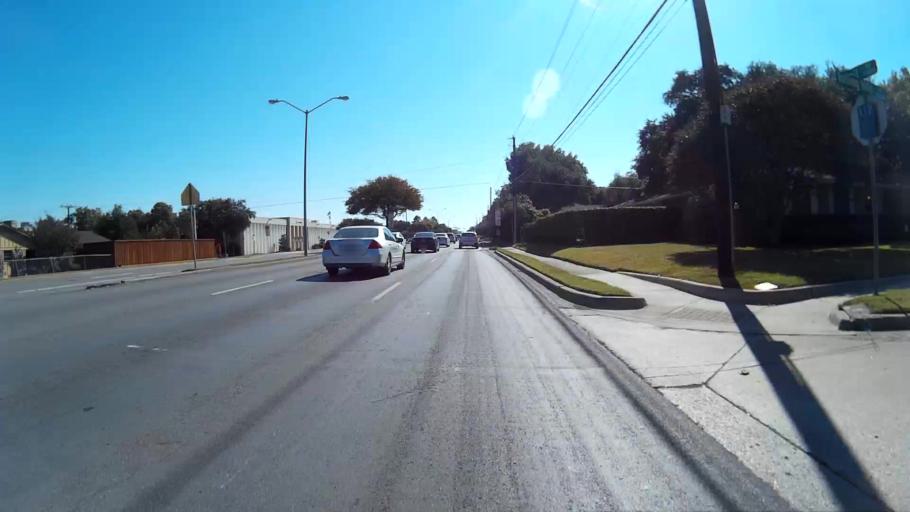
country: US
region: Texas
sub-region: Dallas County
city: Richardson
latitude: 32.9363
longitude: -96.7691
